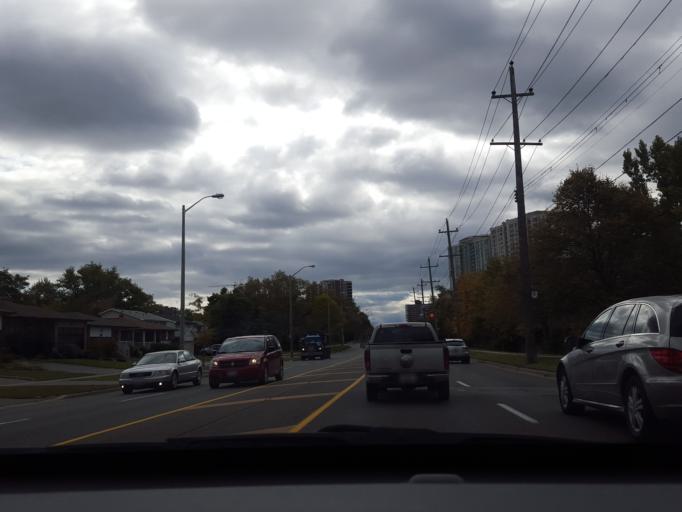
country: CA
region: Ontario
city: Scarborough
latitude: 43.7904
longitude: -79.2916
